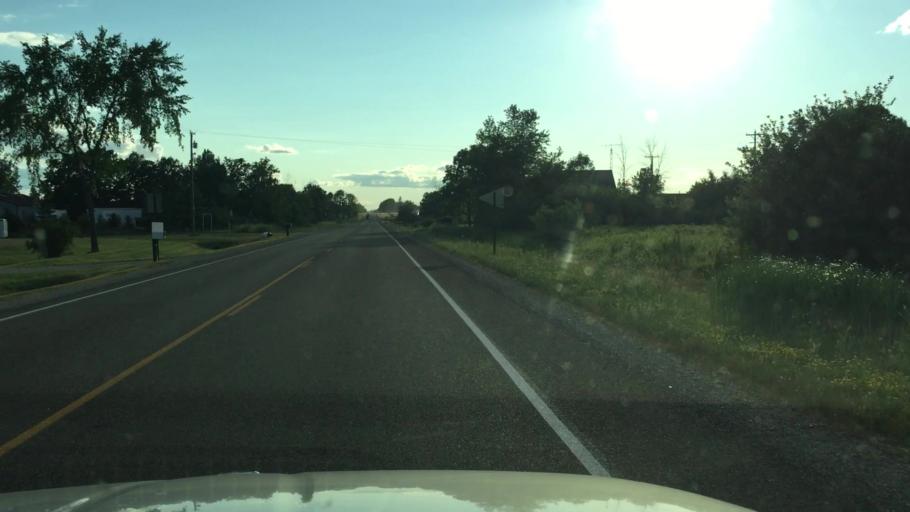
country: US
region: Michigan
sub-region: Saint Clair County
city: Capac
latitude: 43.0270
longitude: -82.9415
